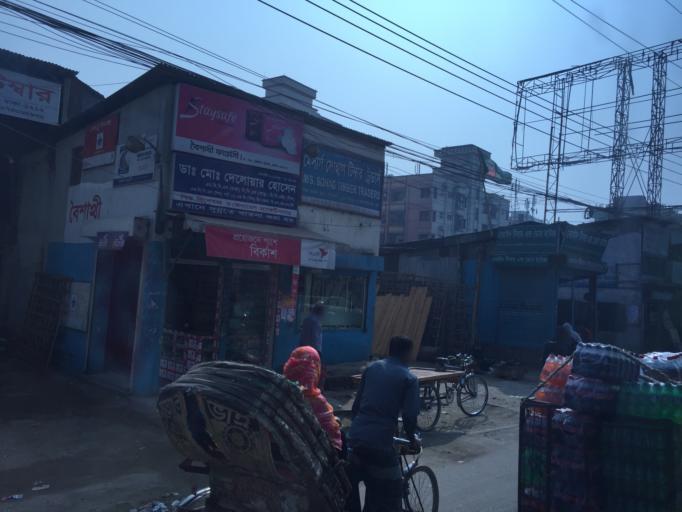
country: BD
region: Dhaka
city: Paltan
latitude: 23.7725
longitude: 90.4257
